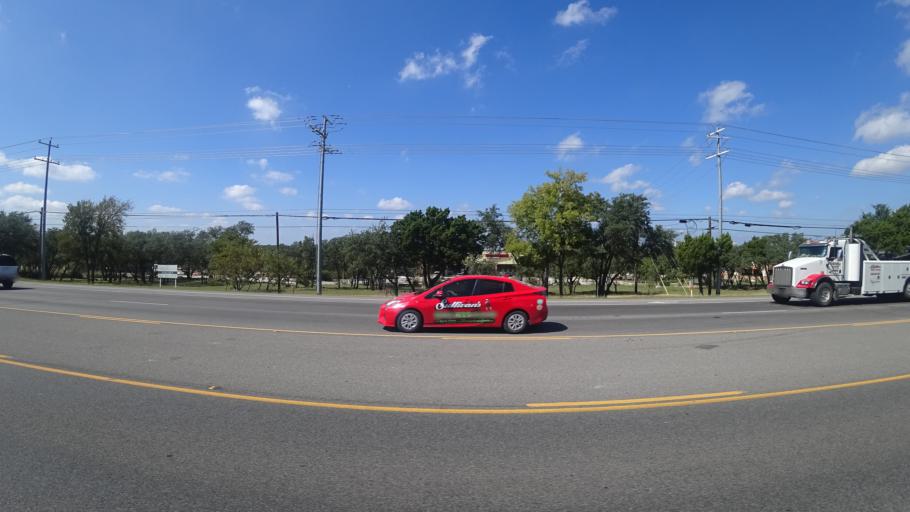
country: US
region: Texas
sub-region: Williamson County
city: Anderson Mill
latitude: 30.4195
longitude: -97.8459
